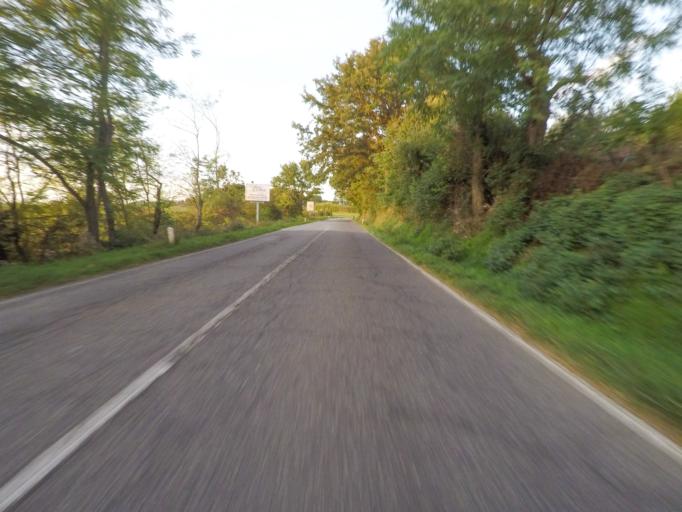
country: IT
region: Tuscany
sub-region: Provincia di Siena
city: Montepulciano
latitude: 43.1266
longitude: 11.7254
